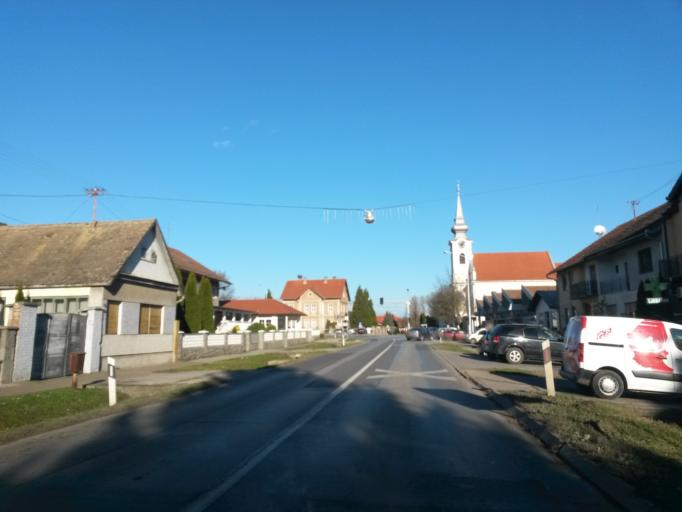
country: HR
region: Osjecko-Baranjska
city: Petrijevci
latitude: 45.6153
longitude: 18.5367
